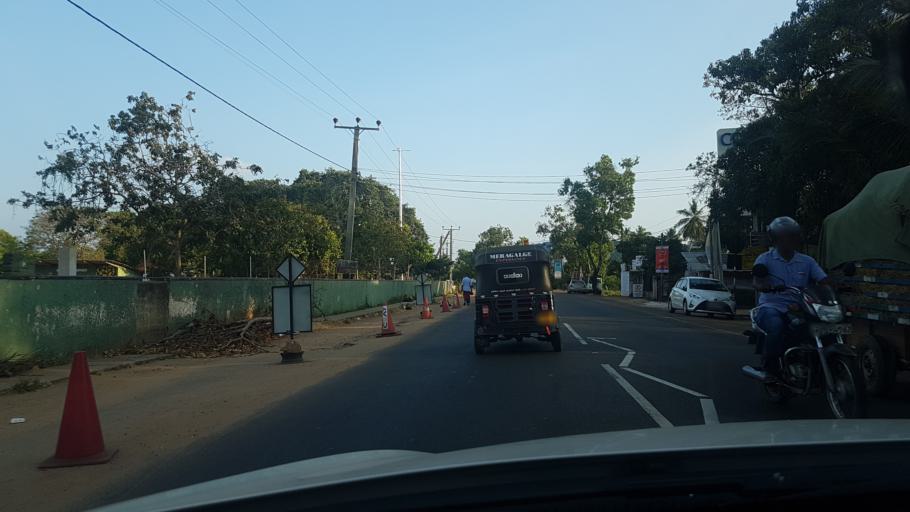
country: LK
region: North Western
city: Chilaw
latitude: 7.5712
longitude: 79.7978
